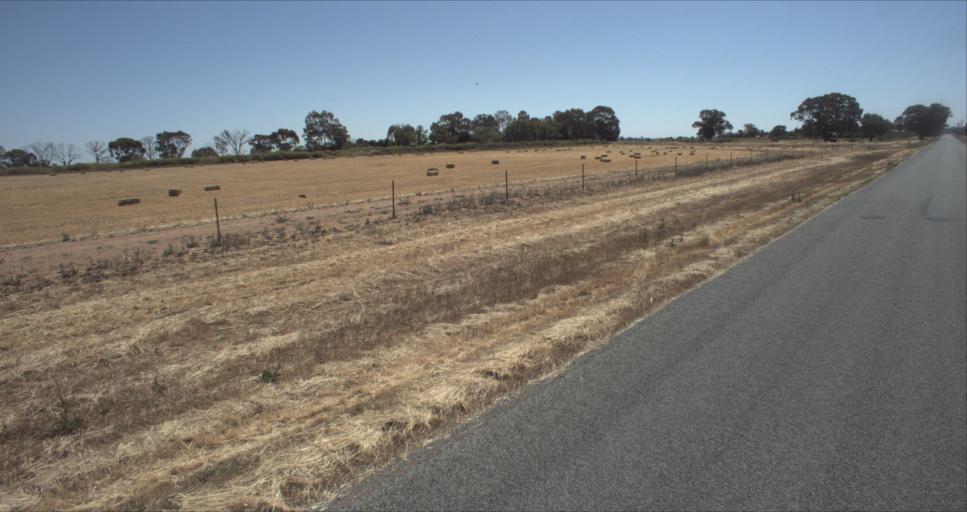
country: AU
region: New South Wales
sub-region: Leeton
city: Leeton
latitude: -34.5321
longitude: 146.4462
